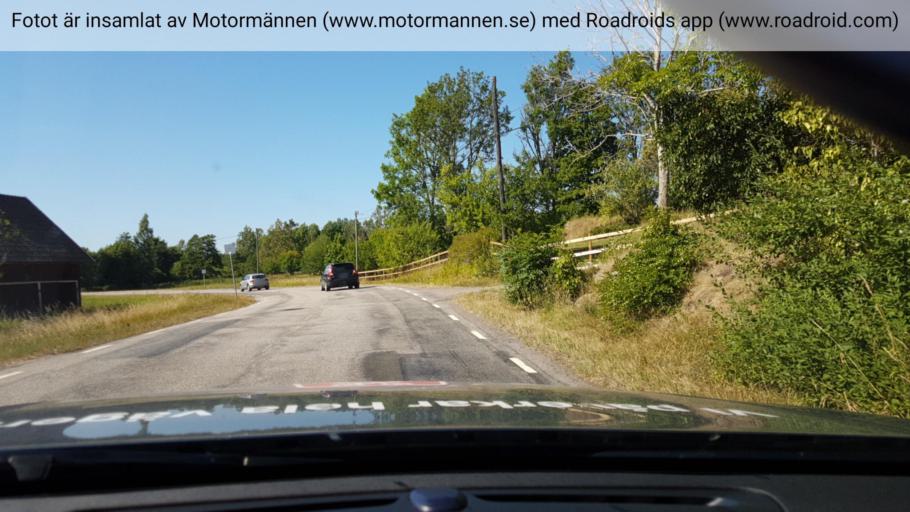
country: SE
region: Vaestra Goetaland
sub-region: Toreboda Kommun
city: Toereboda
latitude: 58.6853
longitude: 14.2041
